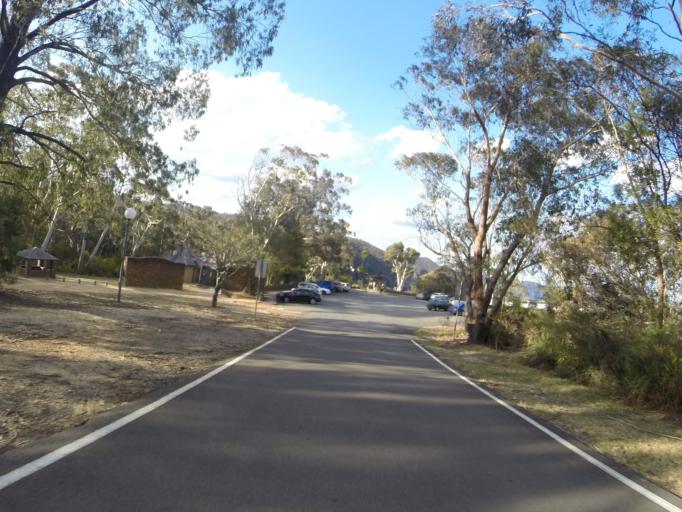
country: AU
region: New South Wales
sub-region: Blue Mountains Municipality
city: Blackheath
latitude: -33.6286
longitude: 150.3107
